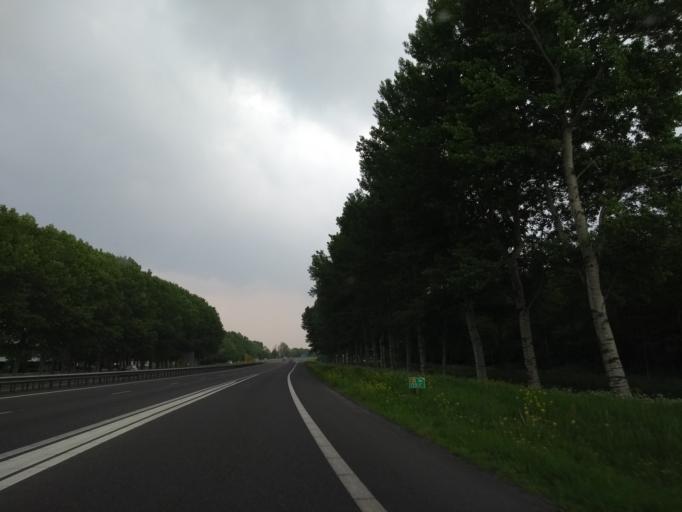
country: NL
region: Friesland
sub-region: Sudwest Fryslan
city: Oppenhuizen
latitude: 53.0199
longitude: 5.6809
